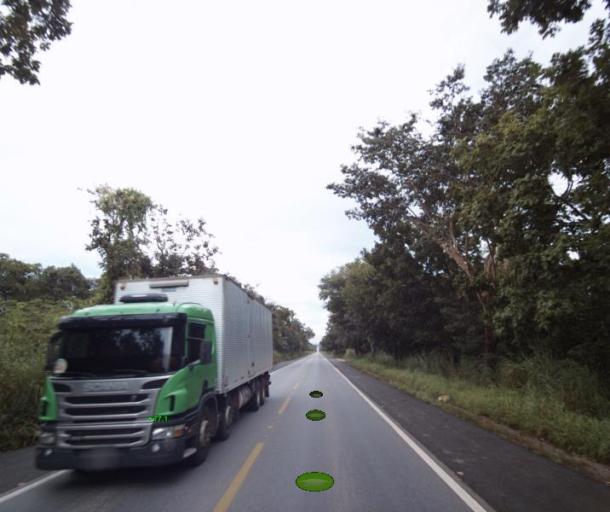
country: BR
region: Goias
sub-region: Porangatu
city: Porangatu
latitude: -13.4935
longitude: -49.1337
